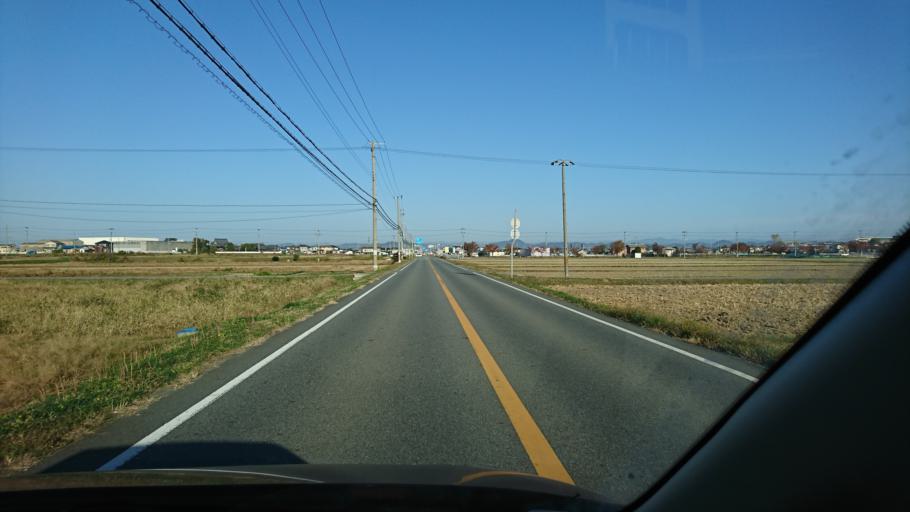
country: JP
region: Hyogo
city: Kakogawacho-honmachi
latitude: 34.7421
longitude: 134.9013
